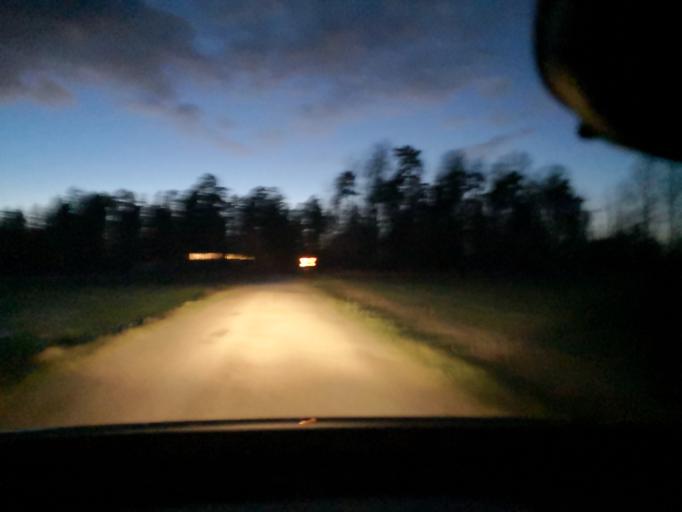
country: SE
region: Uppsala
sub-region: Heby Kommun
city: Heby
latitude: 59.9352
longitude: 16.7437
